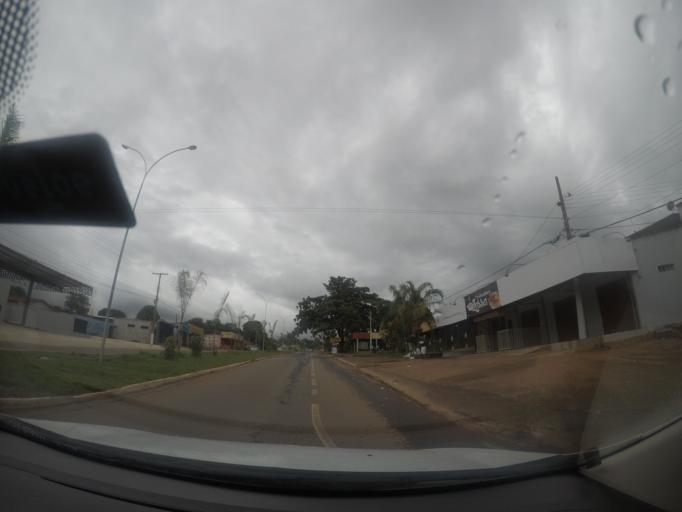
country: BR
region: Goias
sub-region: Trindade
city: Trindade
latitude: -16.6219
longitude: -49.3890
